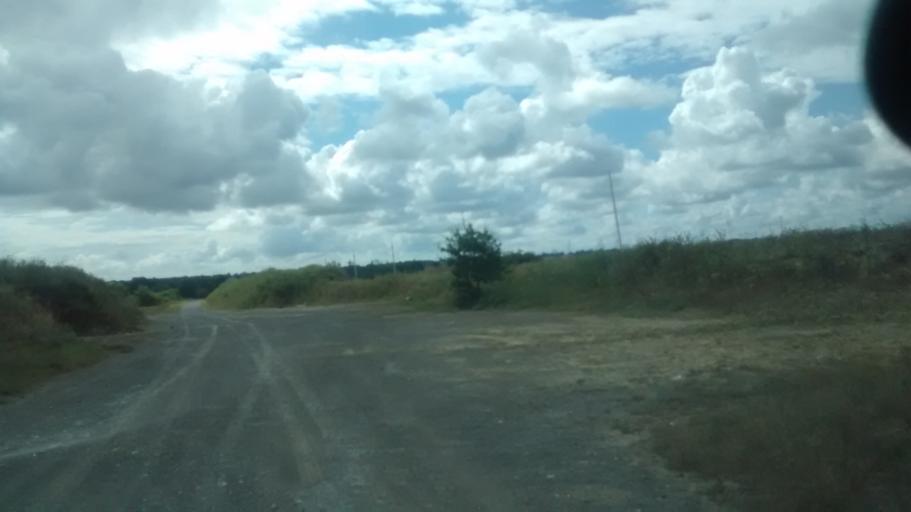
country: FR
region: Brittany
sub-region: Departement d'Ille-et-Vilaine
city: La Dominelais
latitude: 47.7789
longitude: -1.7247
